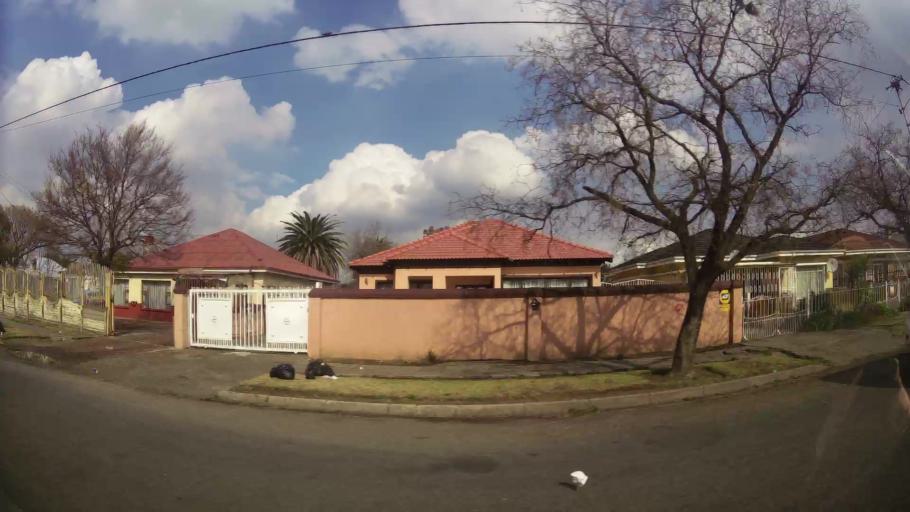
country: ZA
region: Gauteng
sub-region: Sedibeng District Municipality
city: Vereeniging
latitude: -26.6709
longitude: 27.9242
